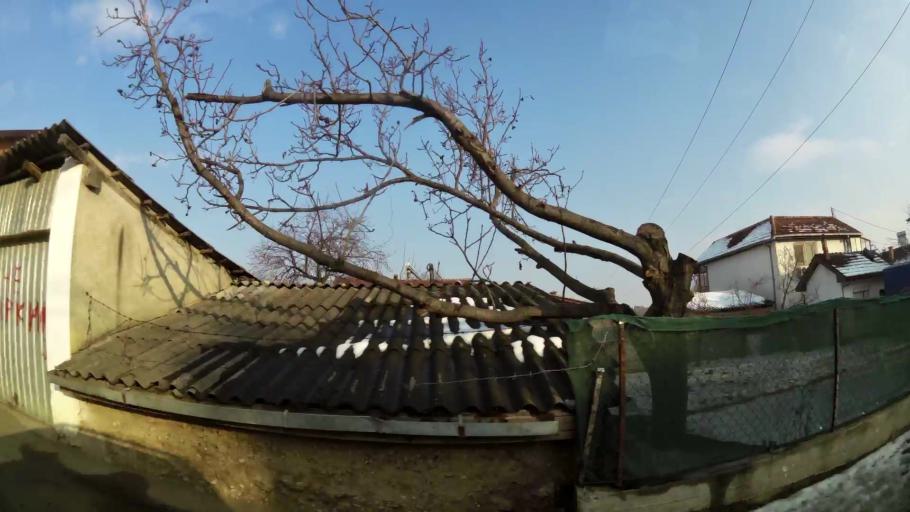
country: MK
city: Creshevo
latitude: 42.0297
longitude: 21.5176
